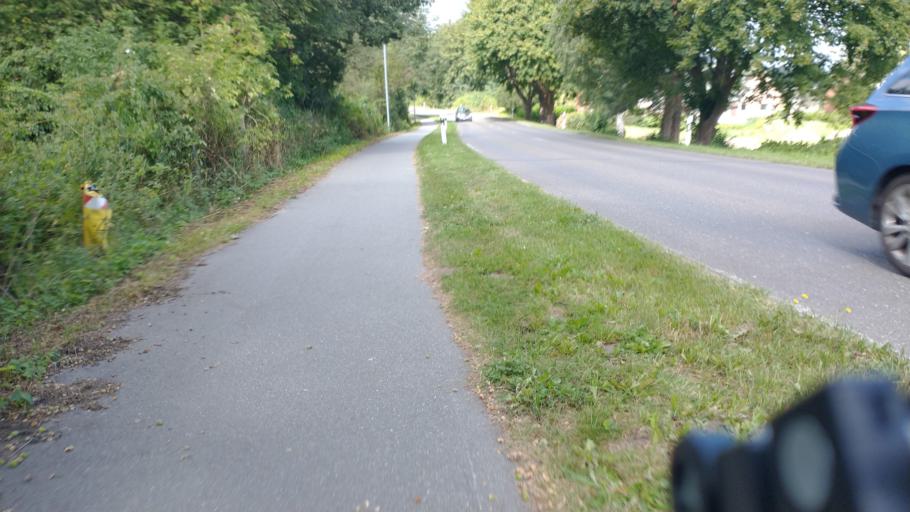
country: DE
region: Schleswig-Holstein
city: Bad Oldesloe
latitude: 53.8109
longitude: 10.3482
